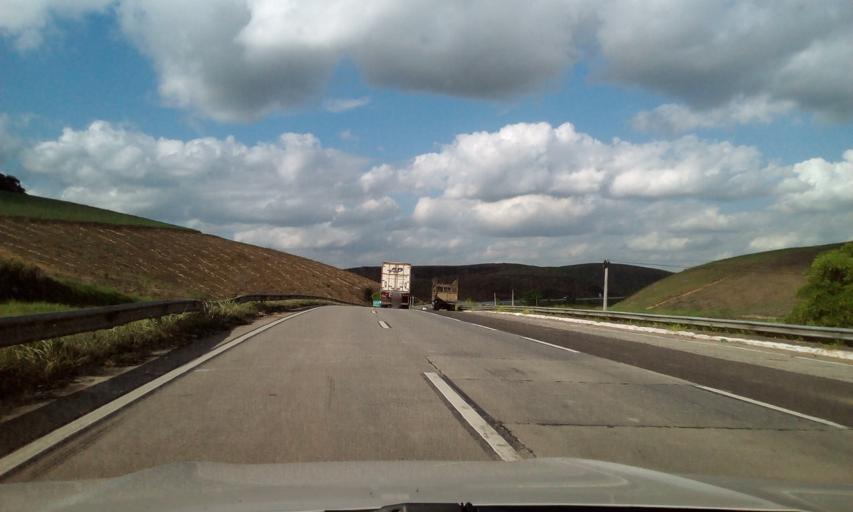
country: BR
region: Pernambuco
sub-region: Joaquim Nabuco
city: Joaquim Nabuco
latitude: -8.6304
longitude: -35.5597
